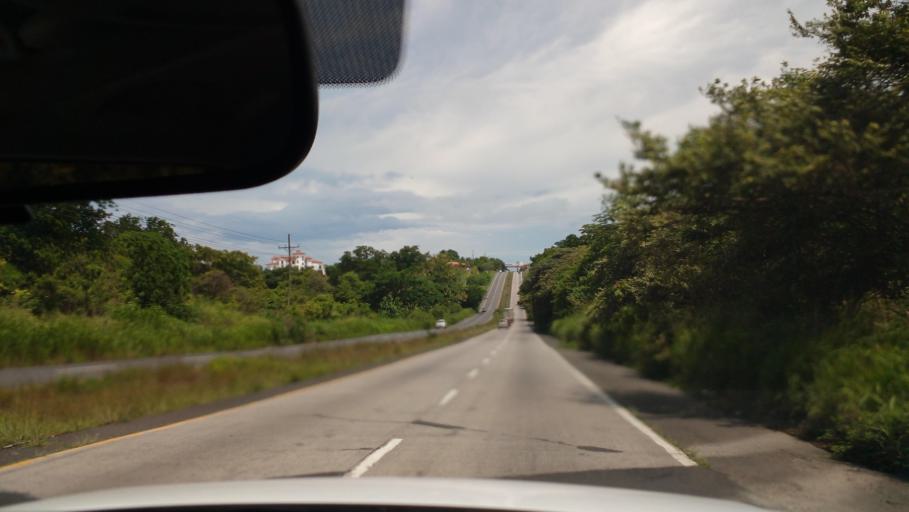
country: PA
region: Panama
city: Nueva Gorgona
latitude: 8.4950
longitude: -79.9582
